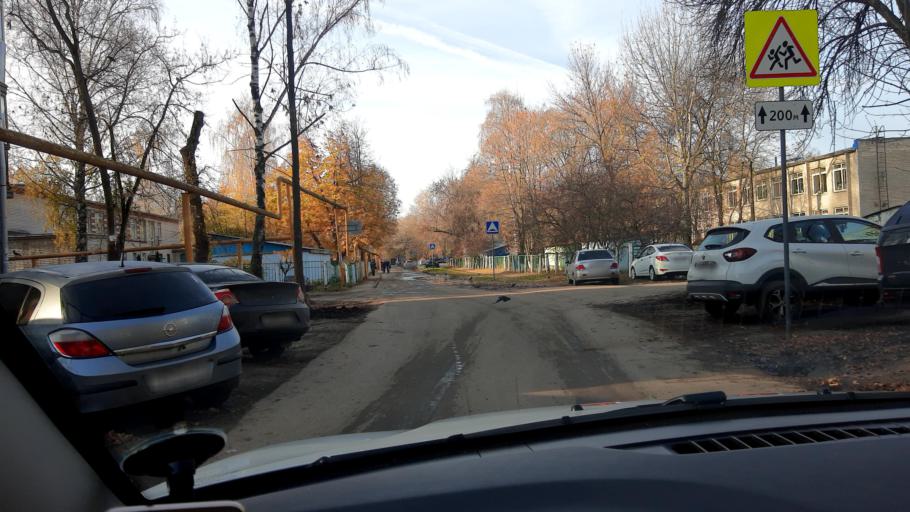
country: RU
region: Nizjnij Novgorod
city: Burevestnik
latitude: 56.2352
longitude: 43.8671
